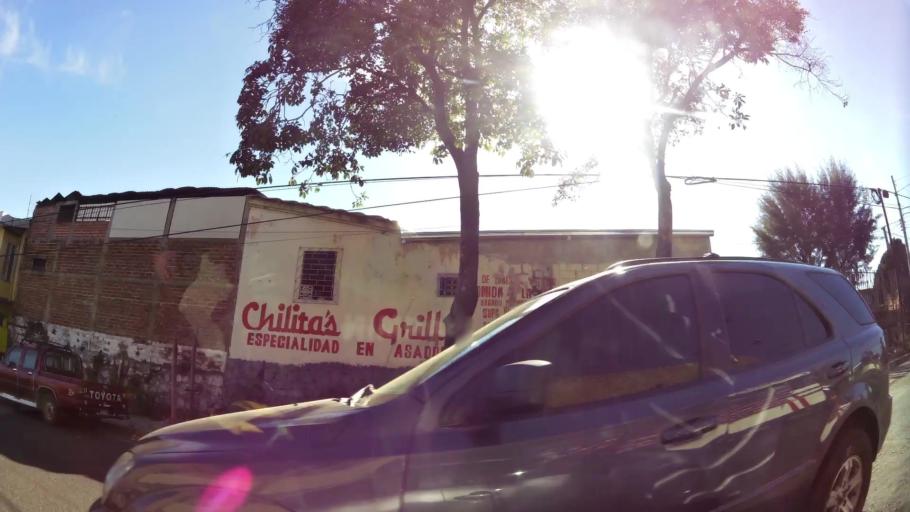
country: SV
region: Santa Ana
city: Santa Ana
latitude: 13.9807
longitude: -89.5677
